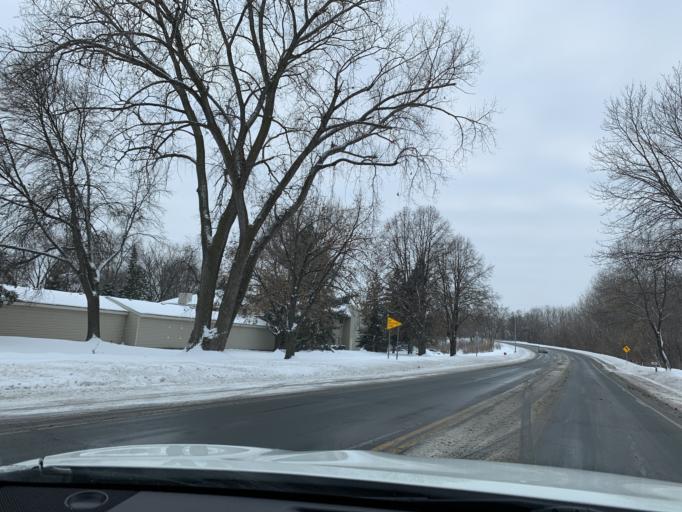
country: US
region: Minnesota
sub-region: Anoka County
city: Coon Rapids
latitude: 45.1638
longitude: -93.2820
